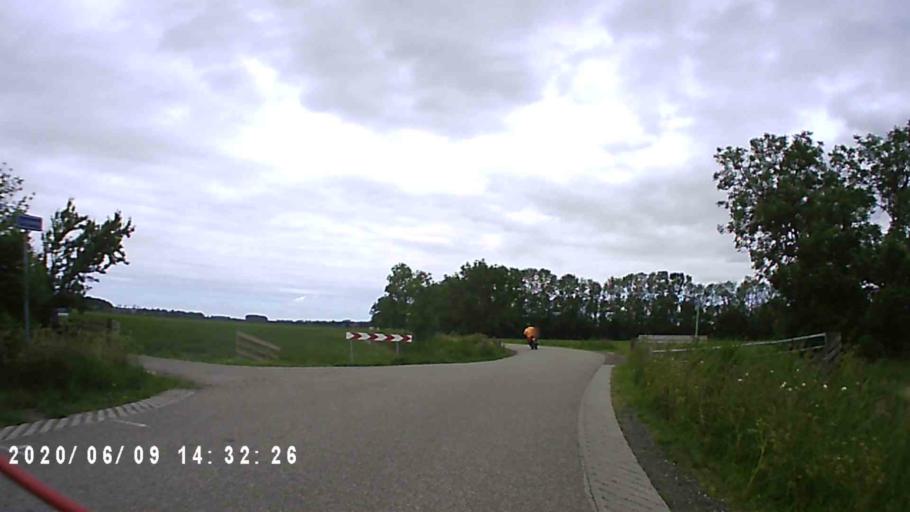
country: NL
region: Groningen
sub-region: Gemeente Bedum
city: Bedum
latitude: 53.3193
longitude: 6.5917
